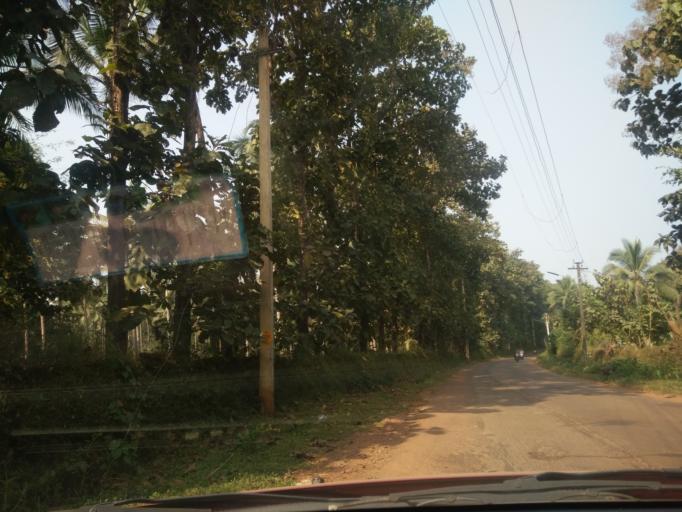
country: IN
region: Goa
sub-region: North Goa
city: Valpoy
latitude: 15.4967
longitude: 74.1445
